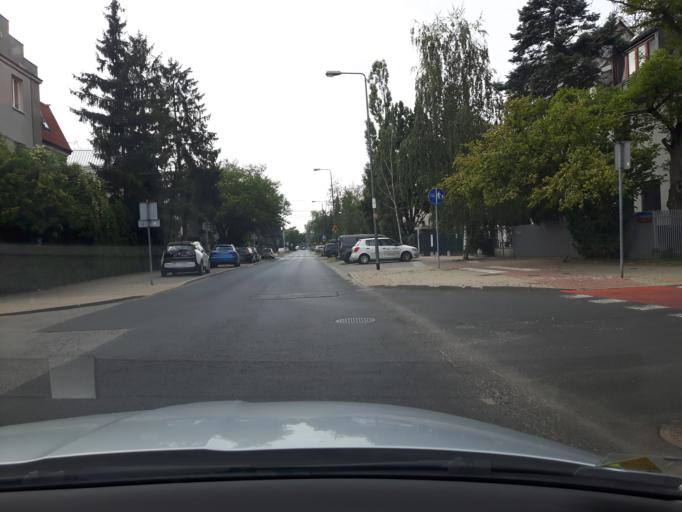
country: PL
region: Masovian Voivodeship
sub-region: Warszawa
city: Mokotow
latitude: 52.1913
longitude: 21.0668
